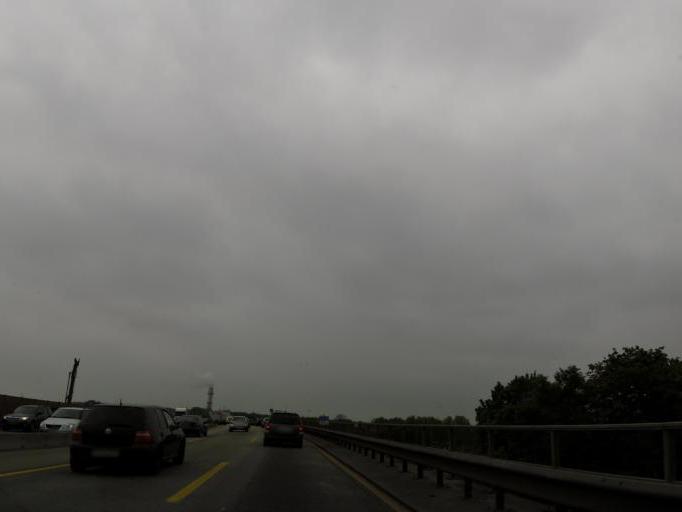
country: DE
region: Hamburg
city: Stellingen
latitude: 53.5913
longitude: 9.9178
